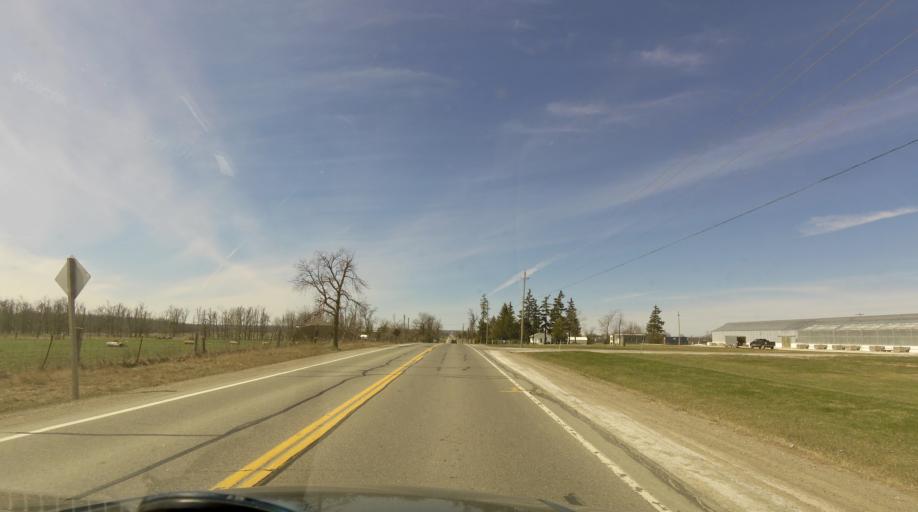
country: CA
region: Ontario
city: Brampton
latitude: 43.6959
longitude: -79.8690
